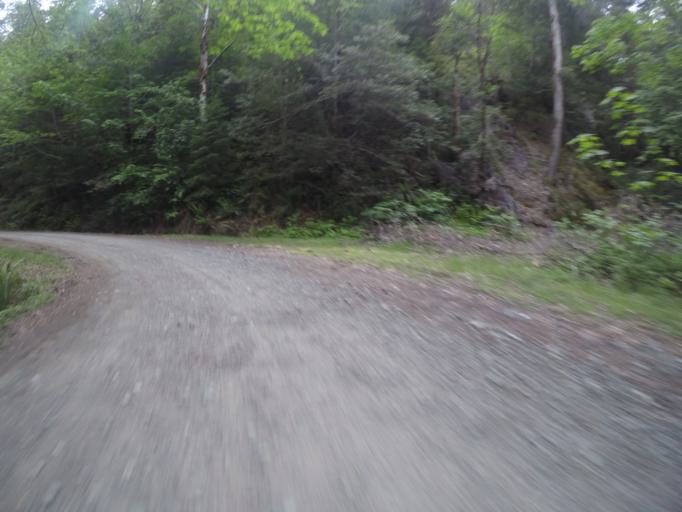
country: US
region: California
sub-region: Del Norte County
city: Bertsch-Oceanview
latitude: 41.7424
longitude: -123.8795
